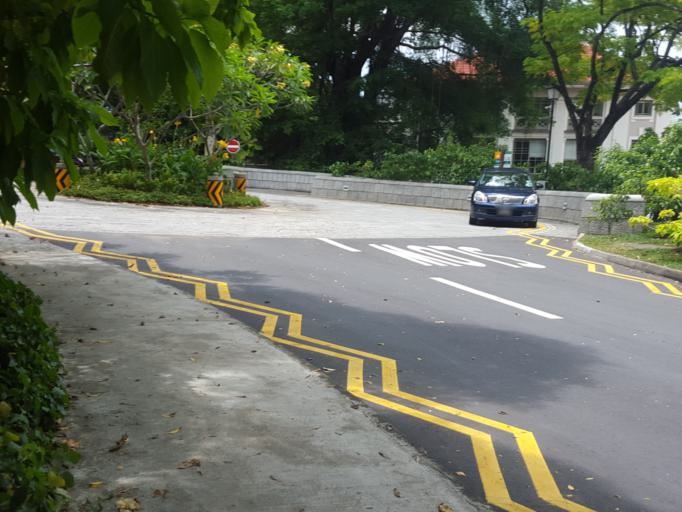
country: SG
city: Singapore
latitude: 1.2965
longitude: 103.8463
